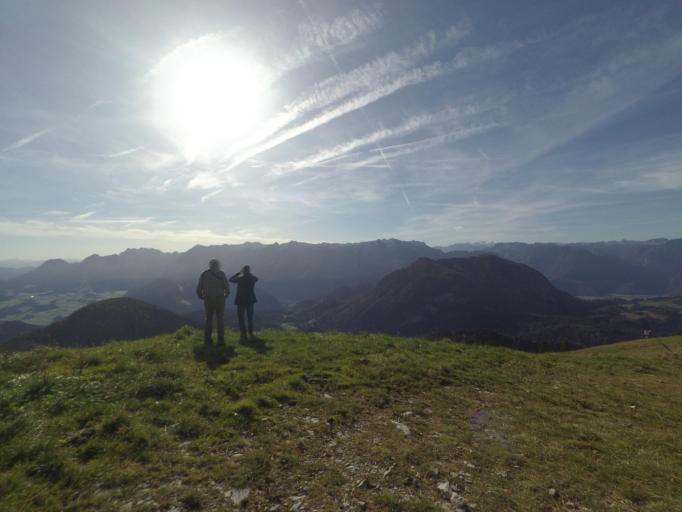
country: AT
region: Salzburg
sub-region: Politischer Bezirk Salzburg-Umgebung
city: Hintersee
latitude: 47.6365
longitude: 13.2667
